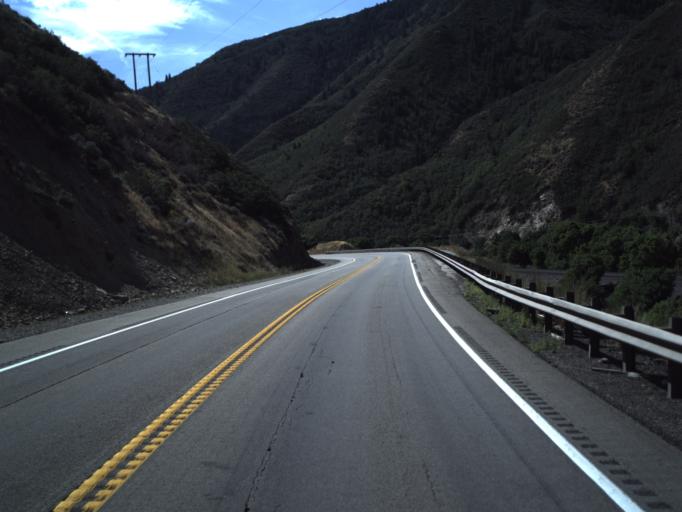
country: US
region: Utah
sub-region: Utah County
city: Mapleton
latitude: 40.0626
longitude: -111.5695
